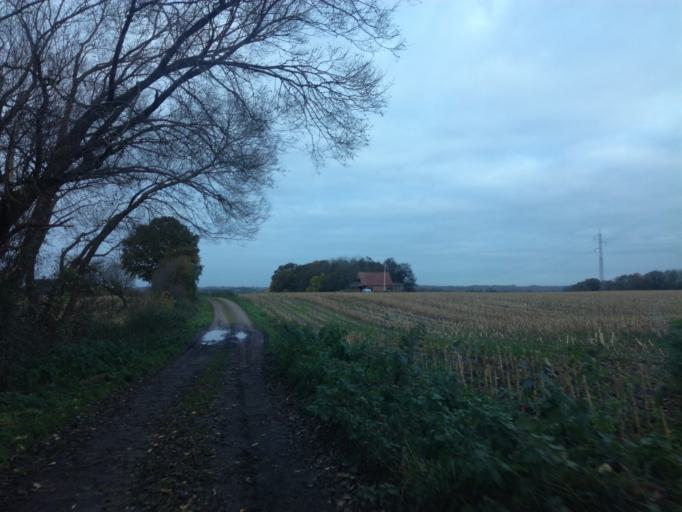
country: DK
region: South Denmark
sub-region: Fredericia Kommune
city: Fredericia
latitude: 55.6104
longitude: 9.7395
